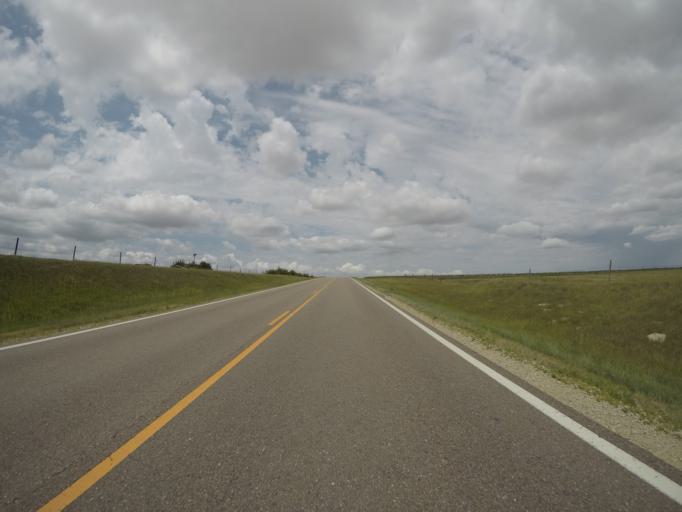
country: US
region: Kansas
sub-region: Rawlins County
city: Atwood
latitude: 39.6991
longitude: -101.0564
